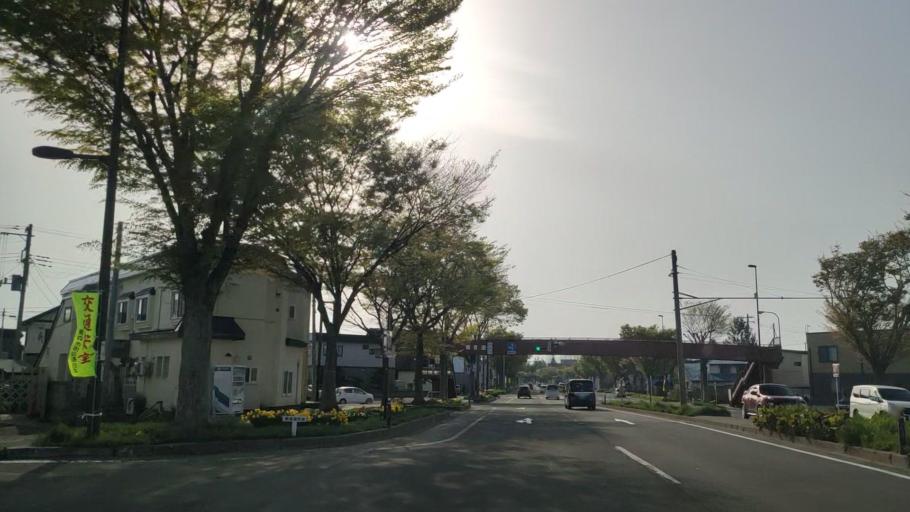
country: JP
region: Aomori
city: Aomori Shi
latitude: 40.8275
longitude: 140.7925
